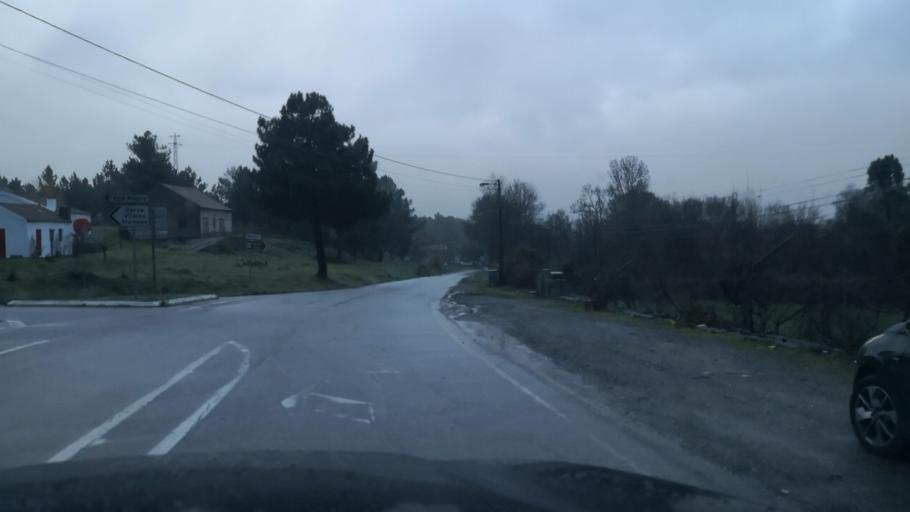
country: PT
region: Vila Real
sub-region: Murca
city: Murca
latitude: 41.3986
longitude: -7.4874
